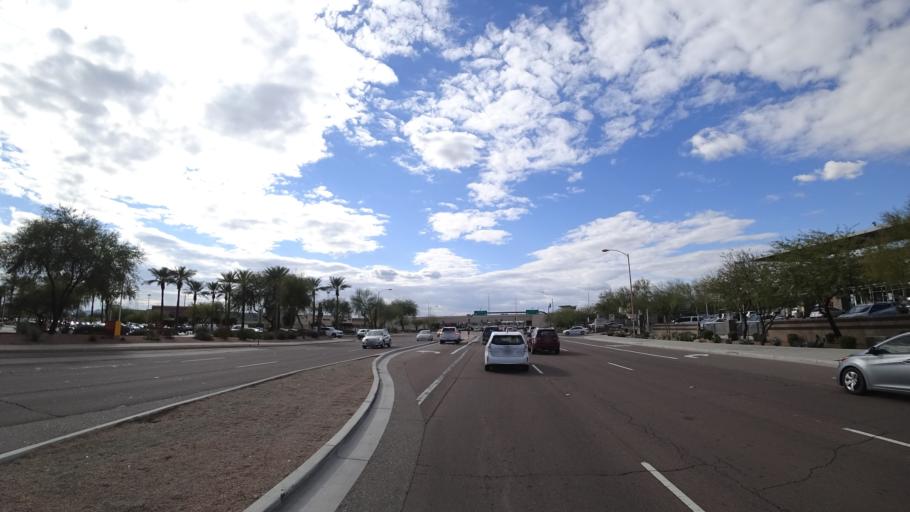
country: US
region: Arizona
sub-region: Maricopa County
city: Paradise Valley
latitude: 33.6298
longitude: -111.8875
